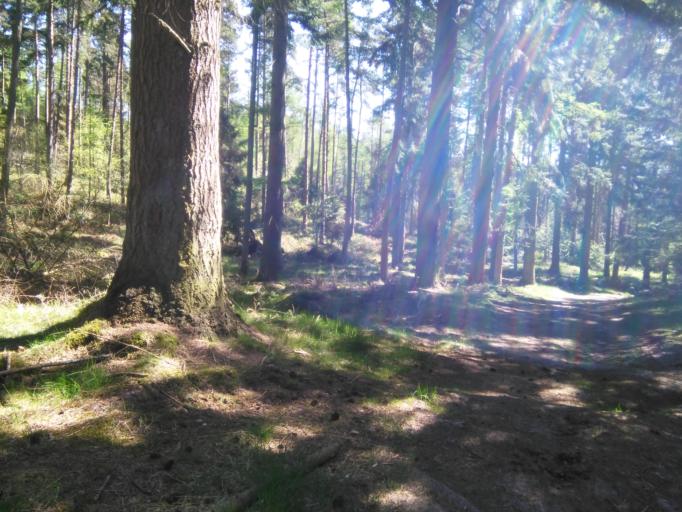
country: DK
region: Central Jutland
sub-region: Odder Kommune
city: Odder
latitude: 55.8900
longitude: 10.0845
